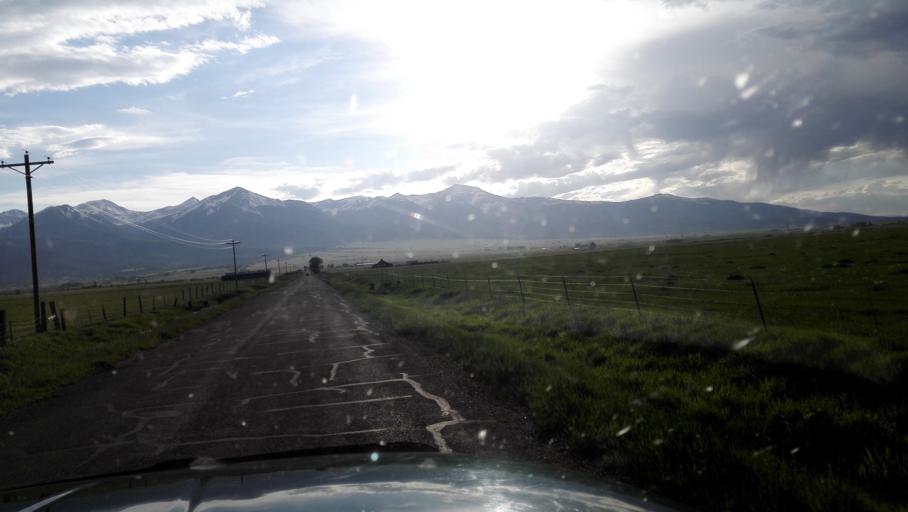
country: US
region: Colorado
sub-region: Custer County
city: Westcliffe
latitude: 38.1316
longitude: -105.4910
